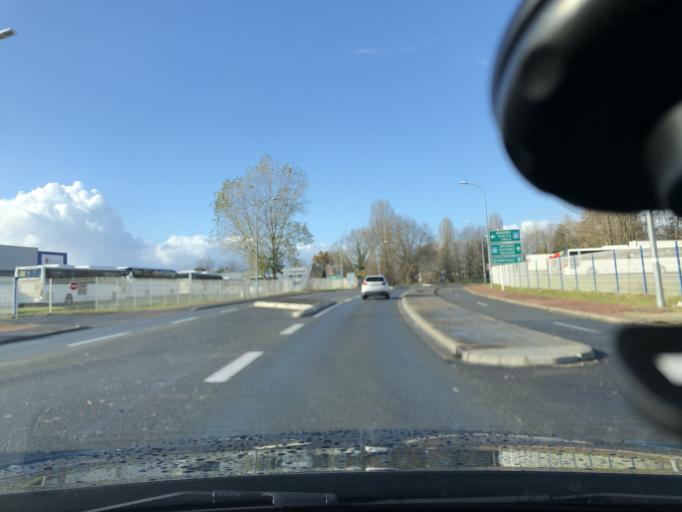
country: FR
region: Aquitaine
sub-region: Departement de la Gironde
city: Bruges
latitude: 44.8871
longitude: -0.5974
